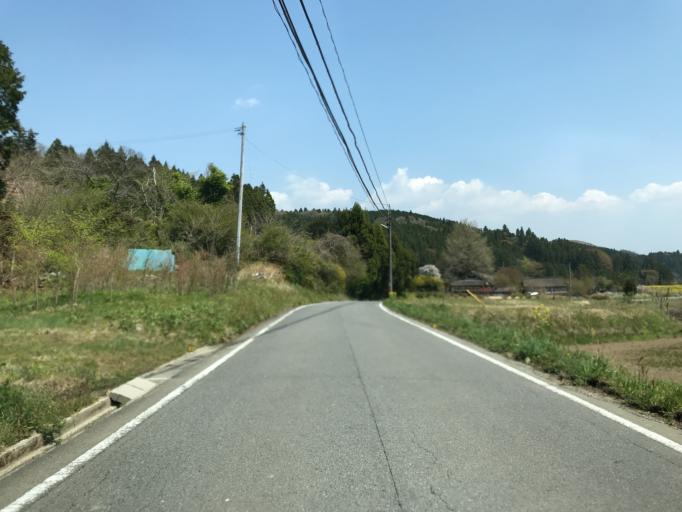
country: JP
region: Ibaraki
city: Kitaibaraki
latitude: 36.9701
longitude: 140.6478
